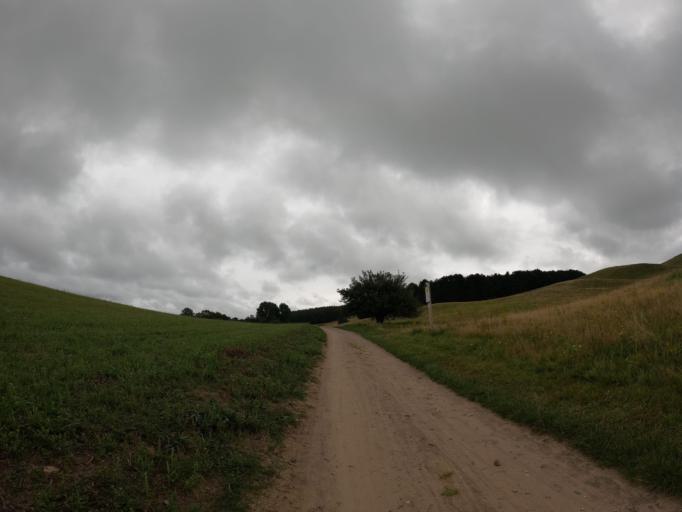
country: DE
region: Mecklenburg-Vorpommern
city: Ostseebad Gohren
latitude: 54.3064
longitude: 13.6916
